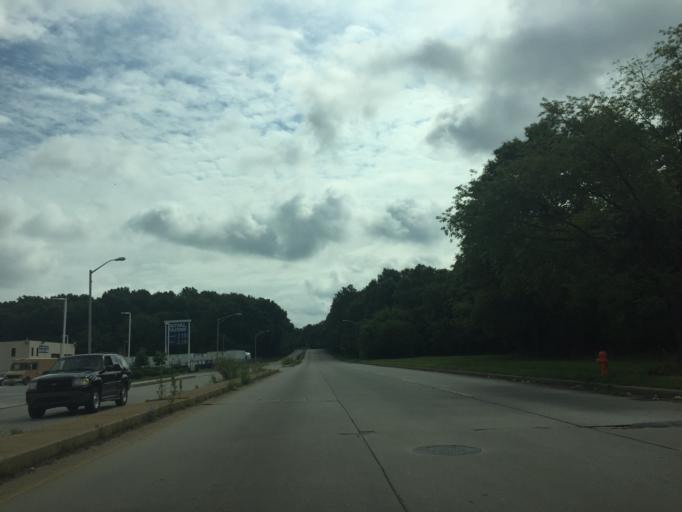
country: US
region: Maryland
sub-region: Anne Arundel County
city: Riviera Beach
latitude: 39.2000
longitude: -76.5556
